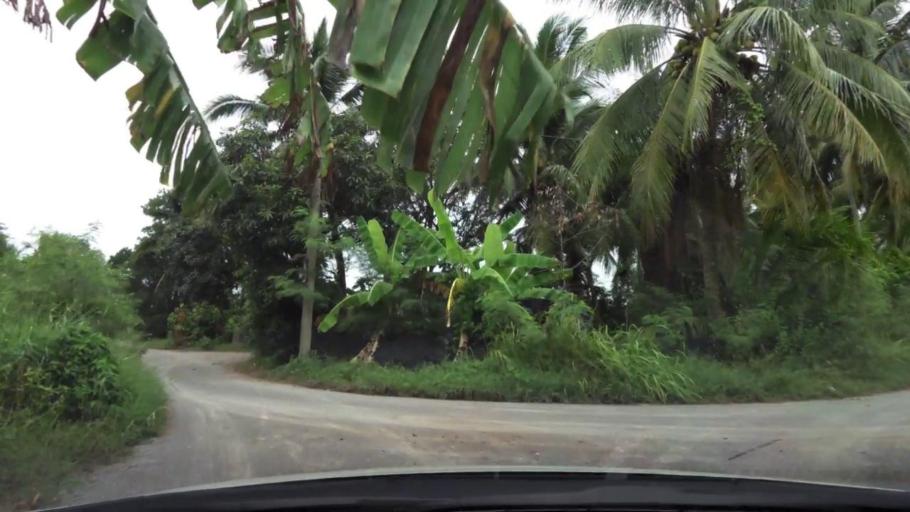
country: TH
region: Samut Sakhon
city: Ban Phaeo
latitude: 13.5928
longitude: 100.0351
